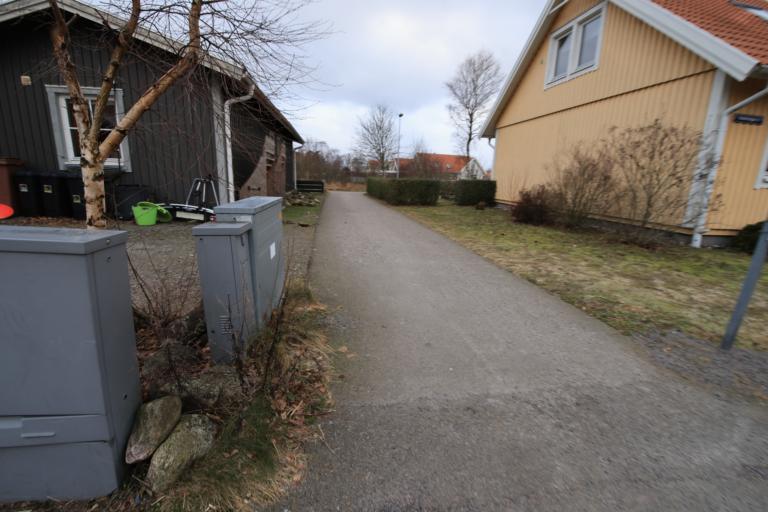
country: SE
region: Halland
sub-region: Varbergs Kommun
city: Traslovslage
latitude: 57.0679
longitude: 12.2883
